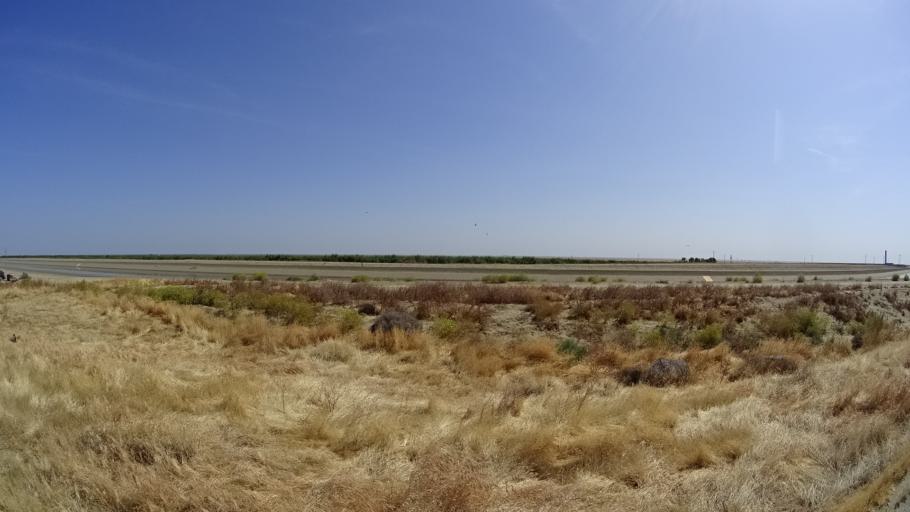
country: US
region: California
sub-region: Kings County
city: Kettleman City
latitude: 36.0502
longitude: -120.0095
